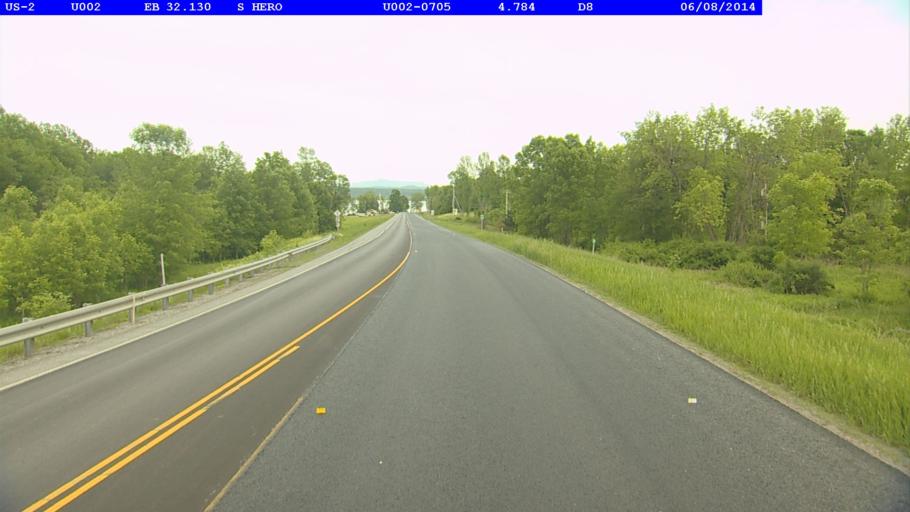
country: US
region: New York
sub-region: Clinton County
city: Cumberland Head
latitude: 44.6382
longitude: -73.2737
